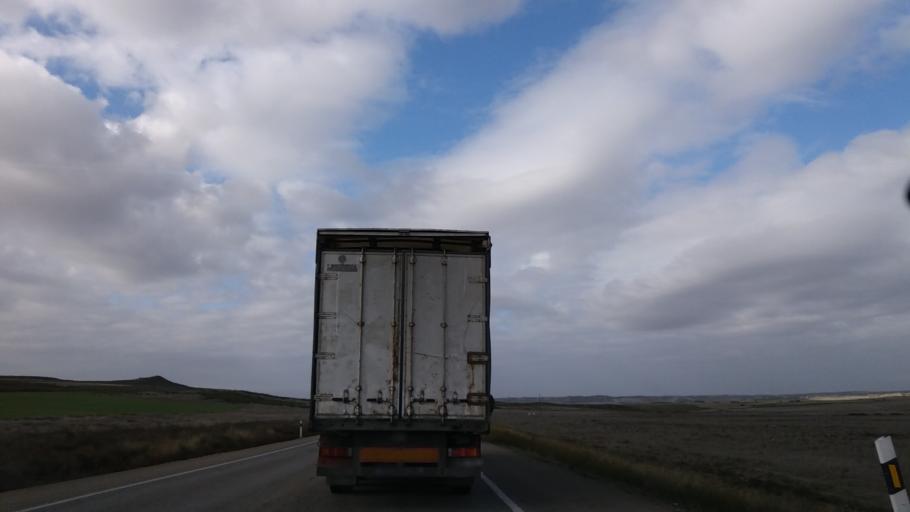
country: ES
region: Aragon
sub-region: Provincia de Zaragoza
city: Pina de Ebro
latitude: 41.5116
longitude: -0.4268
